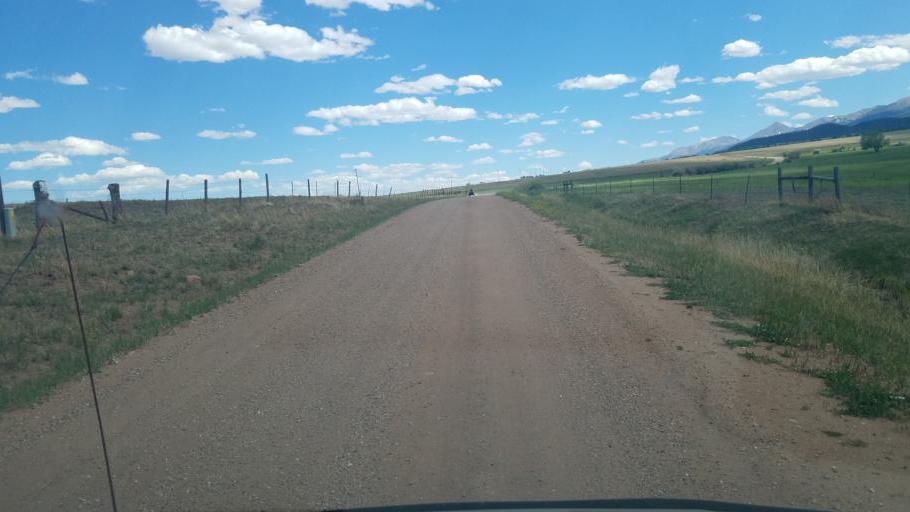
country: US
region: Colorado
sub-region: Custer County
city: Westcliffe
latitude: 38.2565
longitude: -105.6109
